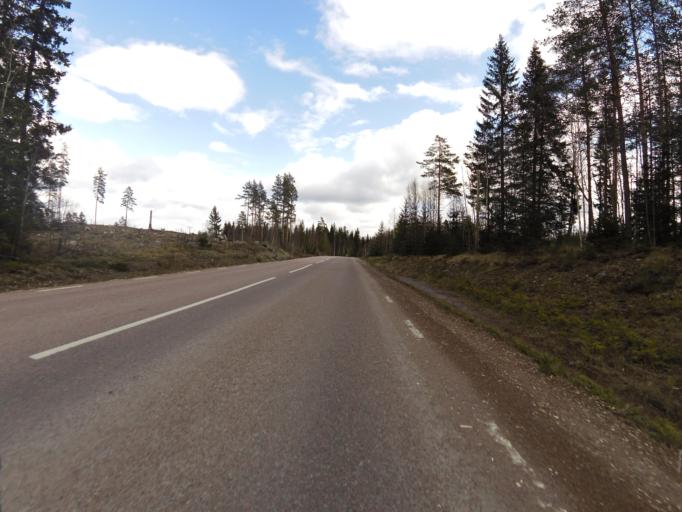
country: SE
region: Dalarna
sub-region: Avesta Kommun
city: Avesta
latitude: 60.3100
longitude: 16.2286
